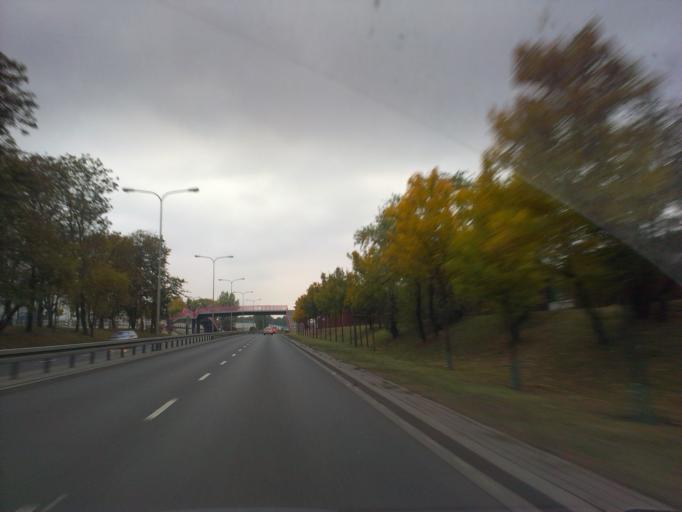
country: PL
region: Greater Poland Voivodeship
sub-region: Poznan
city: Poznan
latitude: 52.4341
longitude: 16.9571
